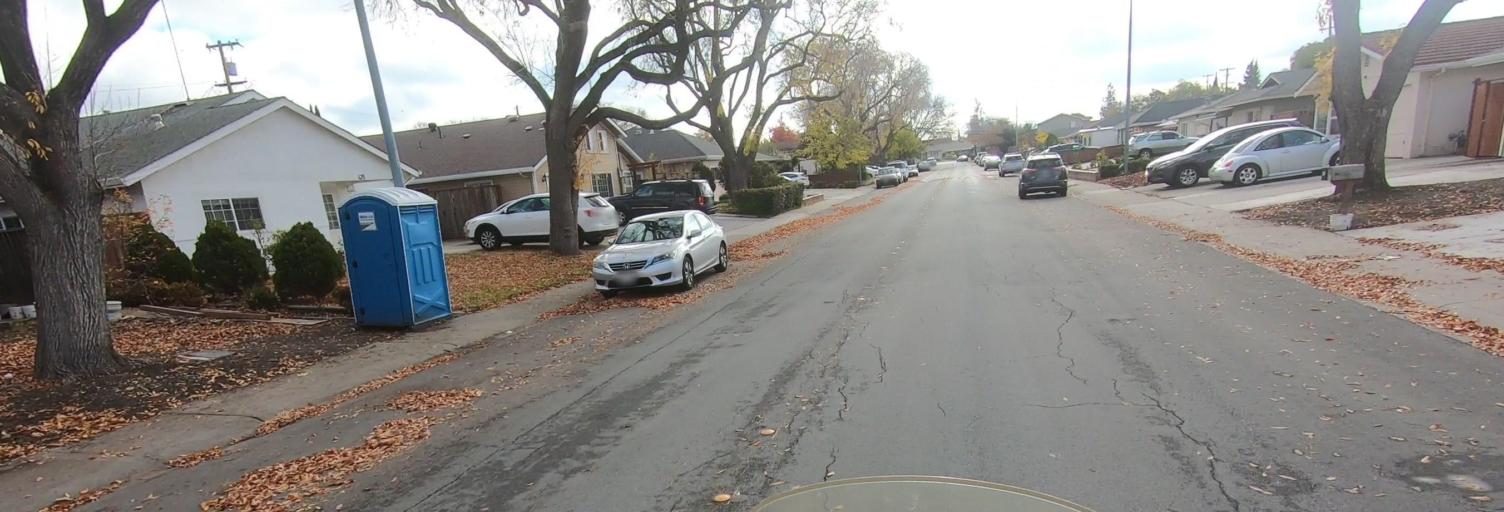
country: US
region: California
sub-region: Santa Clara County
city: Milpitas
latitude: 37.4300
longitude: -121.8796
